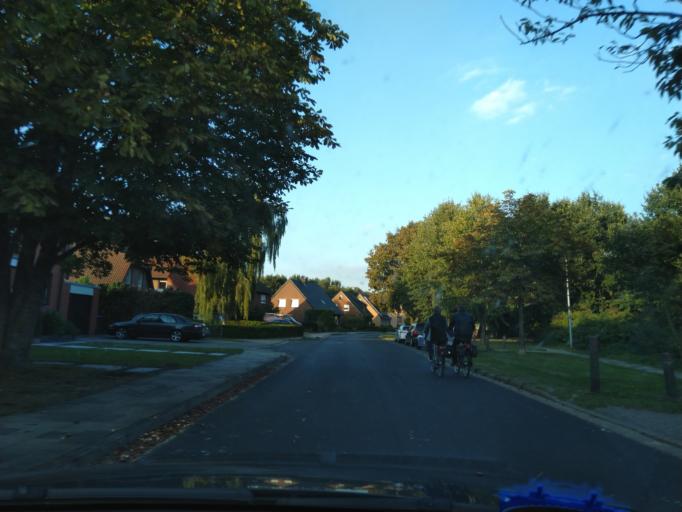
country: DE
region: Lower Saxony
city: Papenburg
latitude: 53.0697
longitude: 7.4355
